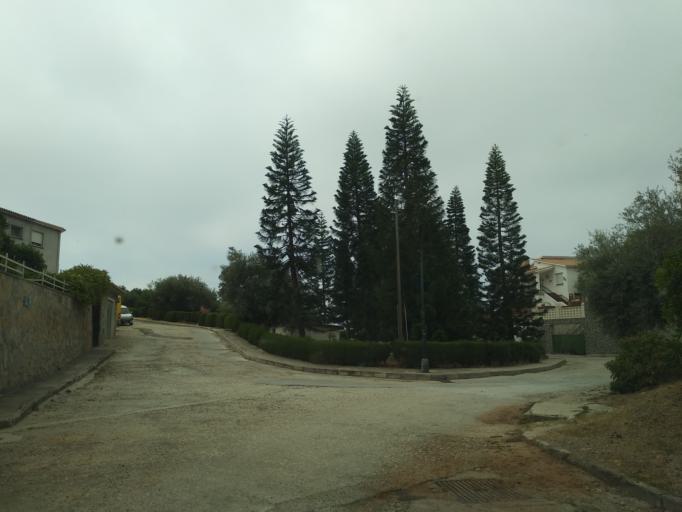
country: ES
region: Andalusia
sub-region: Provincia de Malaga
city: Iznate
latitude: 36.7183
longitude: -4.1894
